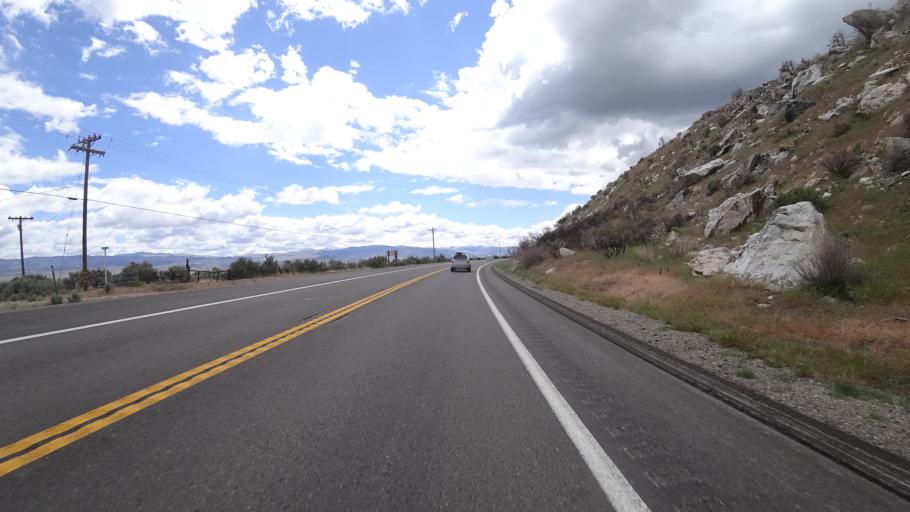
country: US
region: Nevada
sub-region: Lyon County
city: Smith Valley
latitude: 38.6473
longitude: -119.5298
